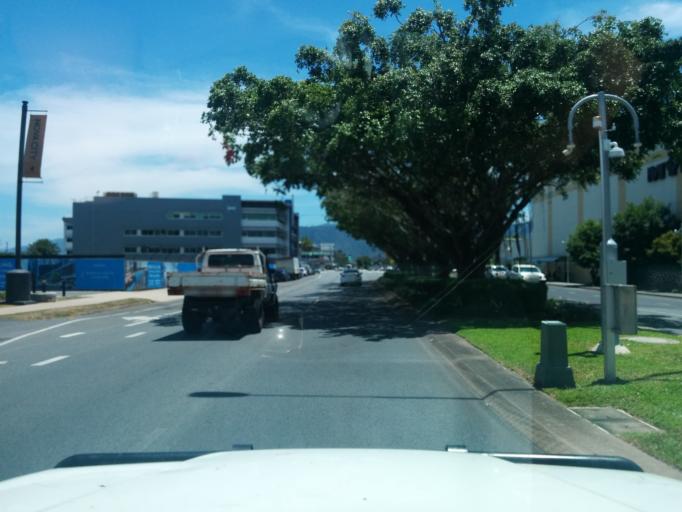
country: AU
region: Queensland
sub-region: Cairns
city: Cairns
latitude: -16.9263
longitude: 145.7741
